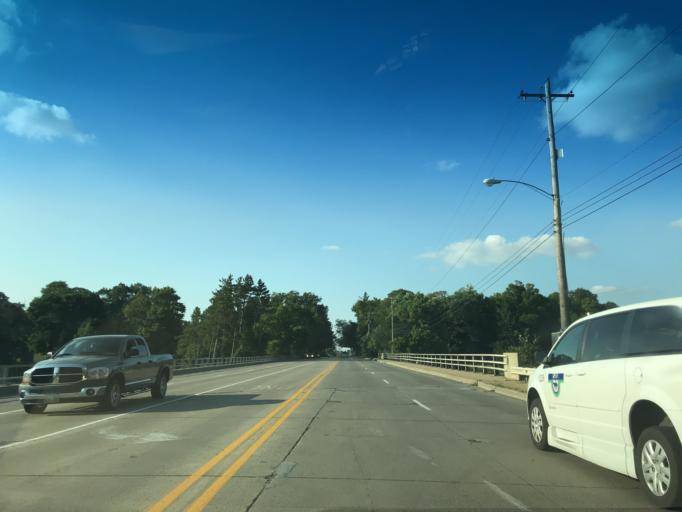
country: US
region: Michigan
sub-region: Eaton County
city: Waverly
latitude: 42.7085
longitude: -84.6030
